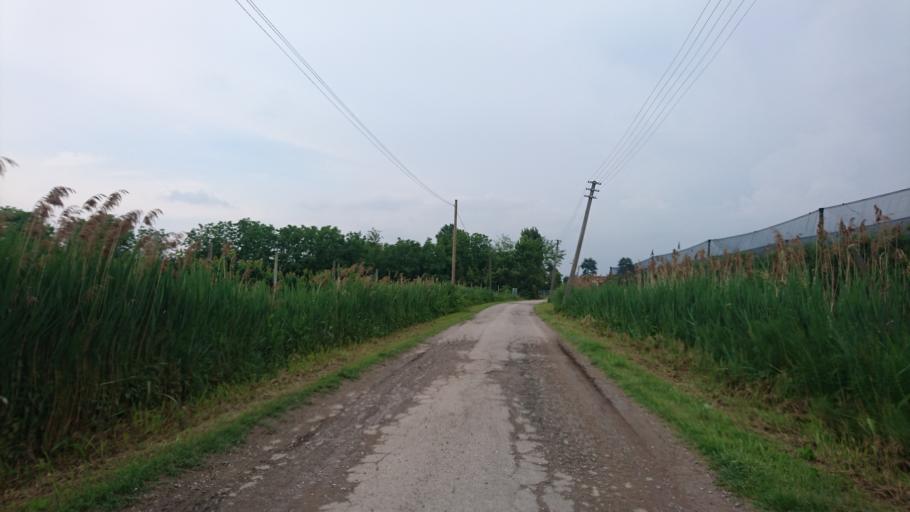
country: IT
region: Veneto
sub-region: Provincia di Rovigo
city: Badia Polesine
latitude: 45.1037
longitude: 11.5006
